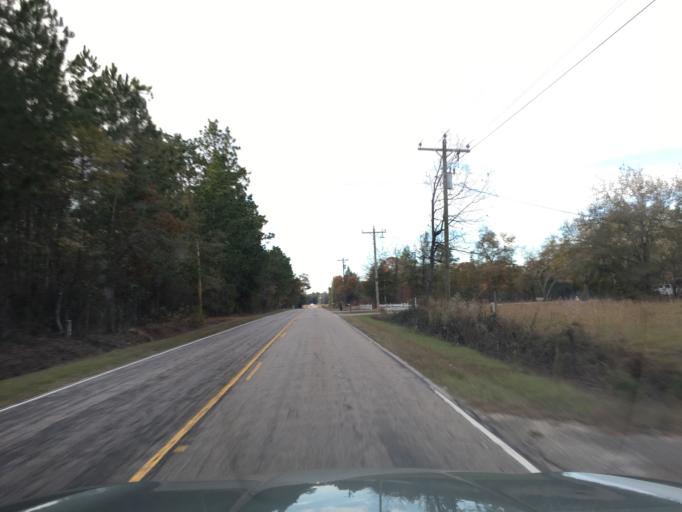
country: US
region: South Carolina
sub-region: Lexington County
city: Red Bank
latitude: 33.7473
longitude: -81.3646
